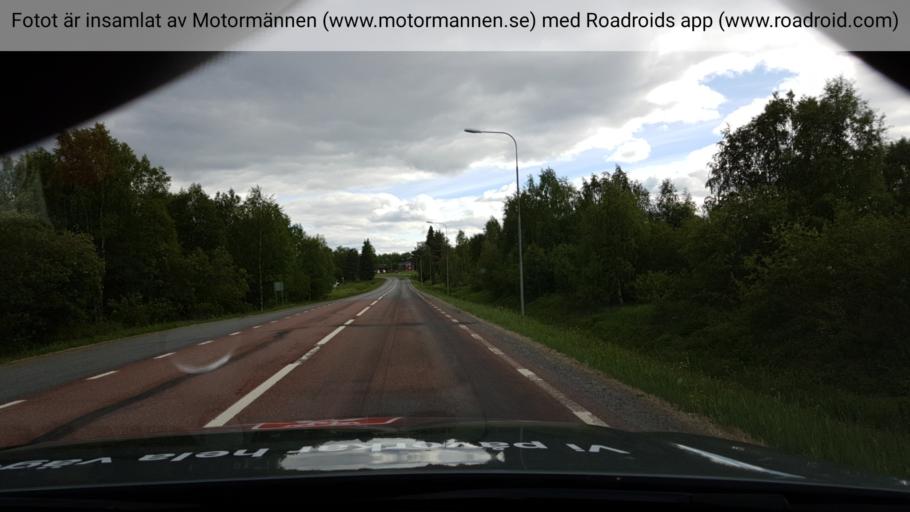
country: SE
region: Jaemtland
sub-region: Stroemsunds Kommun
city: Stroemsund
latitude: 63.8319
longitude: 15.5157
